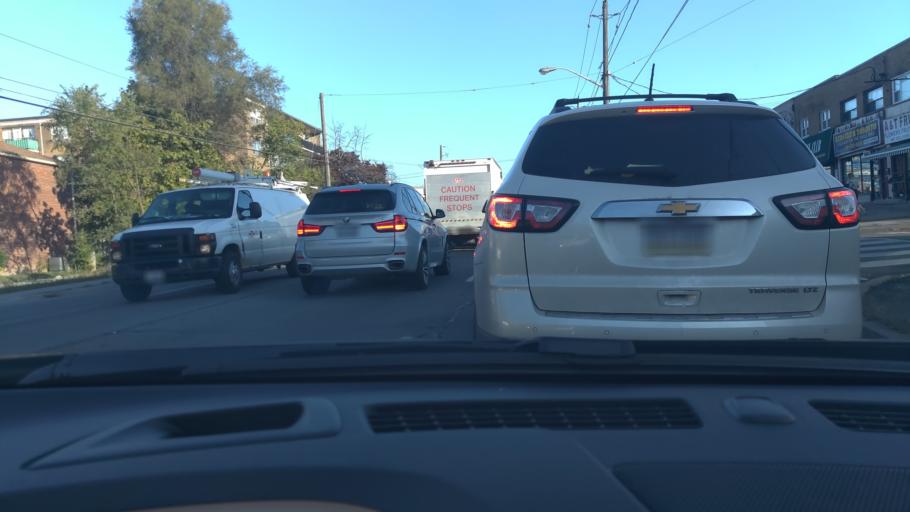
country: CA
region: Ontario
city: Toronto
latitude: 43.7257
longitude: -79.4312
